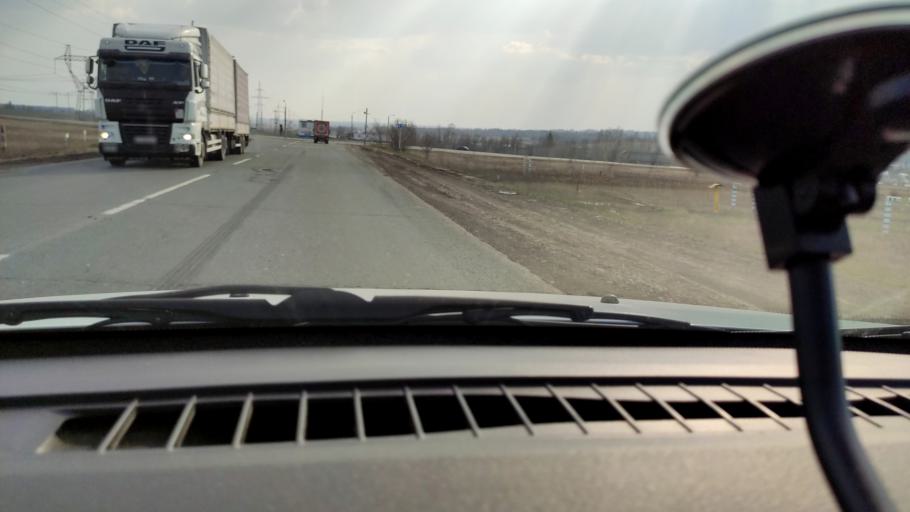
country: RU
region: Samara
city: Dubovyy Umet
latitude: 53.0647
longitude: 50.3776
